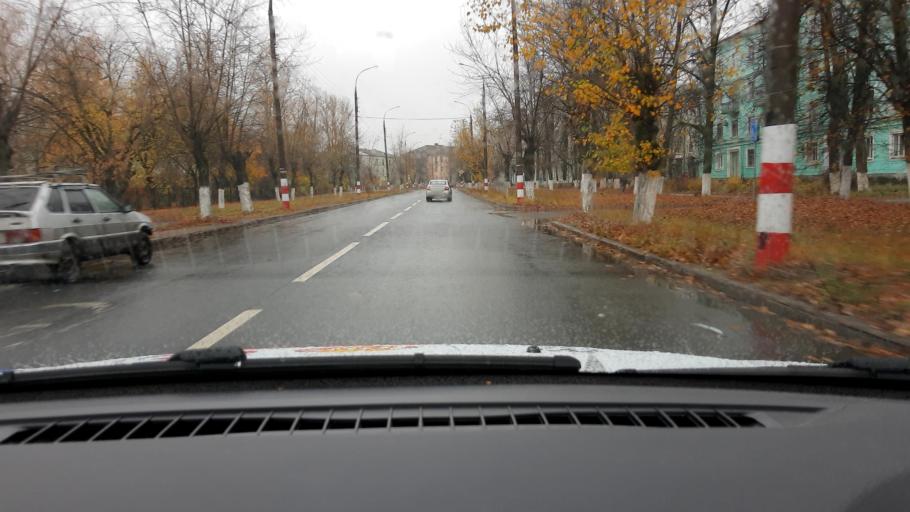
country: RU
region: Nizjnij Novgorod
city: Dzerzhinsk
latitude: 56.2402
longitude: 43.4569
